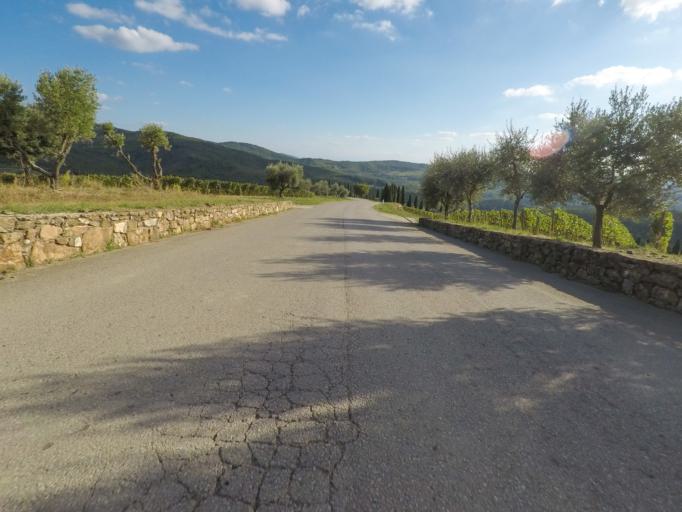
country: IT
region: Tuscany
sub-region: Provincia di Siena
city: Radda in Chianti
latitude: 43.5185
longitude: 11.4040
